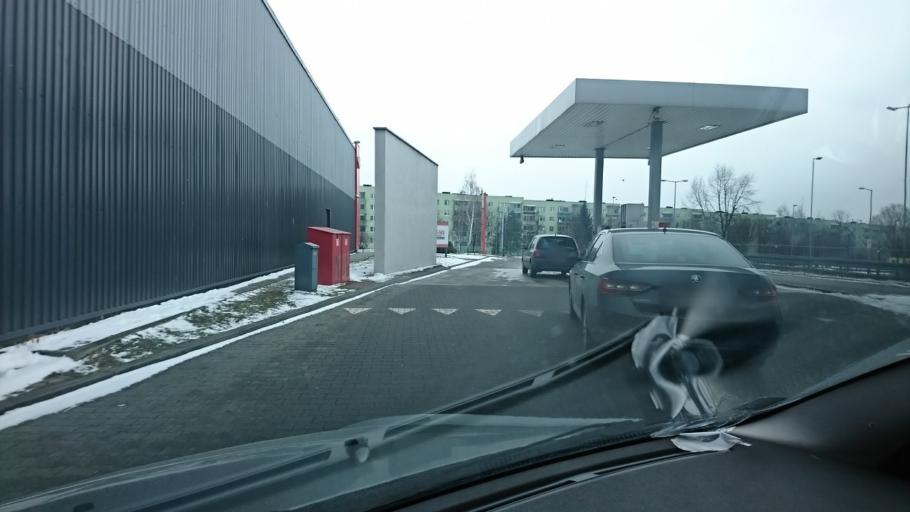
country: PL
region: Lesser Poland Voivodeship
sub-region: Powiat wielicki
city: Czarnochowice
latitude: 50.0148
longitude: 20.0208
